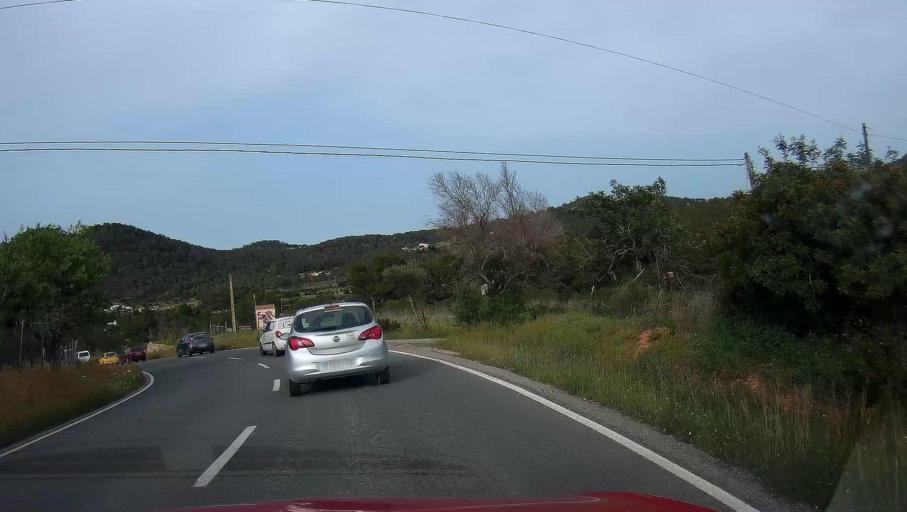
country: ES
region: Balearic Islands
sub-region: Illes Balears
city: Sant Joan de Labritja
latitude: 39.0853
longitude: 1.5009
